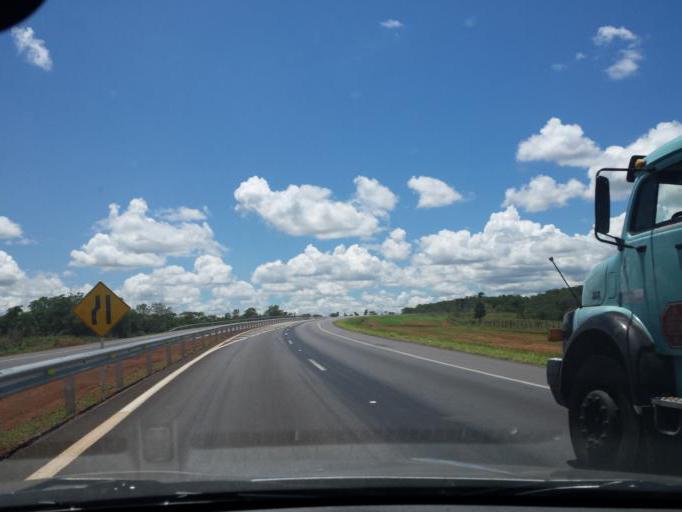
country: BR
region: Goias
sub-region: Cristalina
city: Cristalina
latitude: -16.6280
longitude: -47.7406
